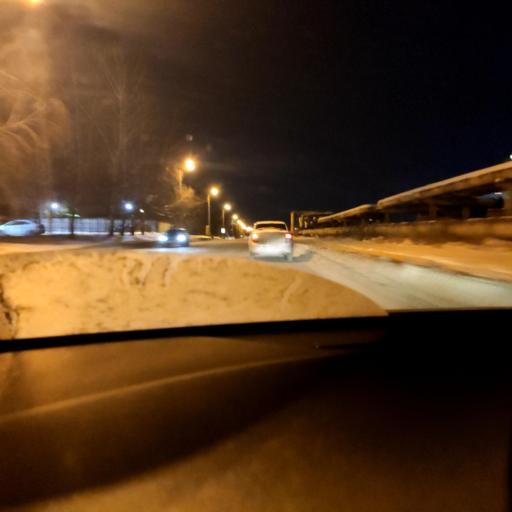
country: RU
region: Tatarstan
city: Staroye Arakchino
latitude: 55.8530
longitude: 49.0256
